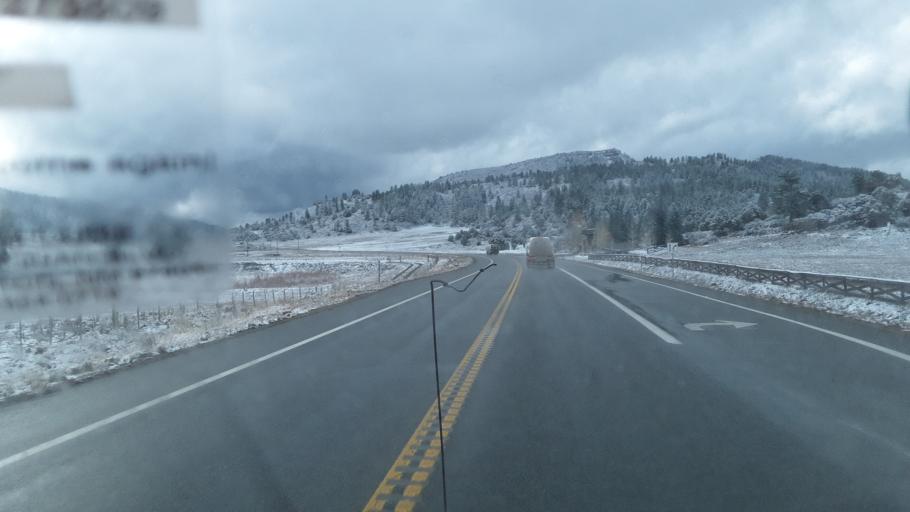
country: US
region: Colorado
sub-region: Archuleta County
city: Pagosa Springs
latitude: 37.2280
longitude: -107.2103
